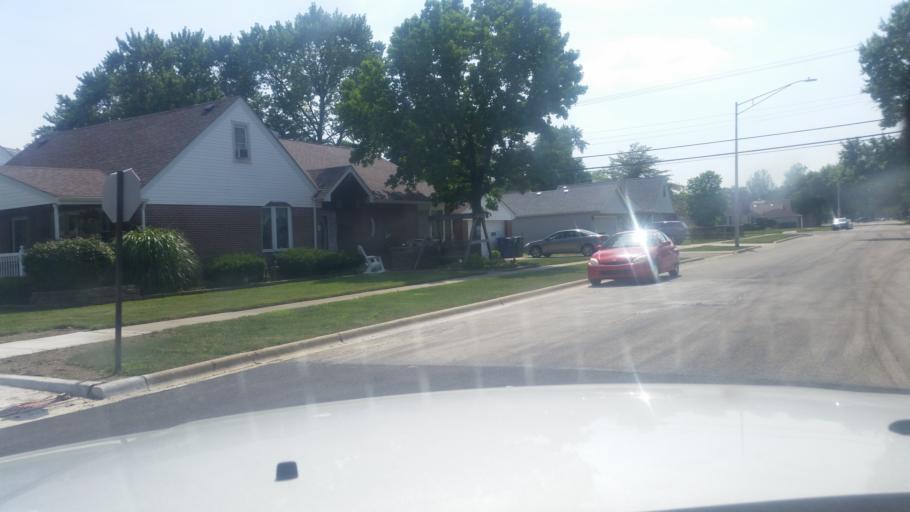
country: US
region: Illinois
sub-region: Cook County
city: Chicago Ridge
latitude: 41.6959
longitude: -87.7694
